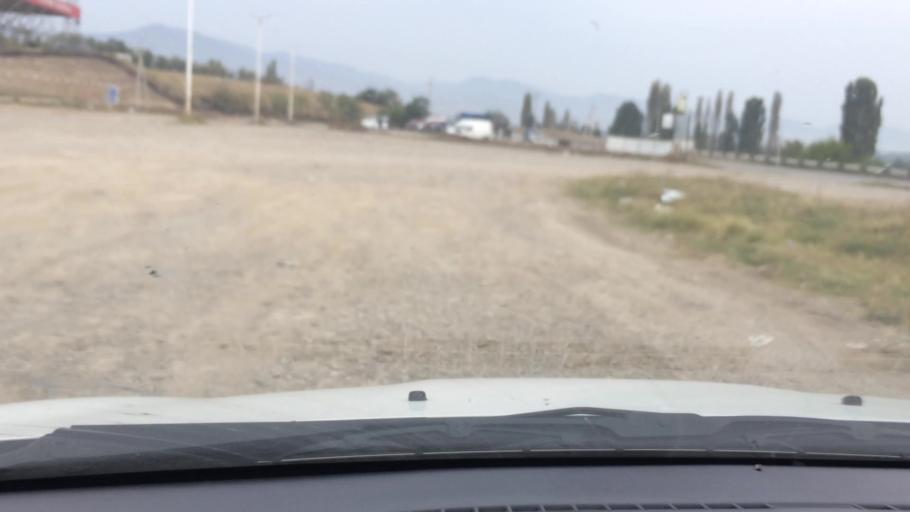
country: AM
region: Tavush
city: Bagratashen
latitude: 41.2319
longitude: 44.8170
